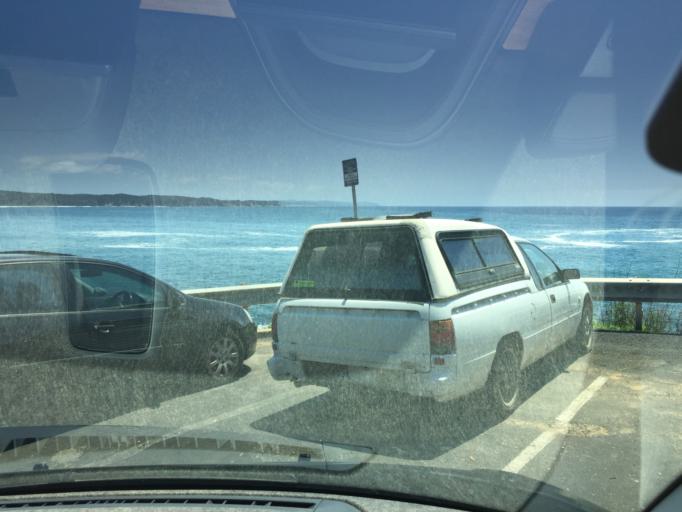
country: AU
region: New South Wales
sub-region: Bega Valley
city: Bega
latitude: -36.7256
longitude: 149.9890
